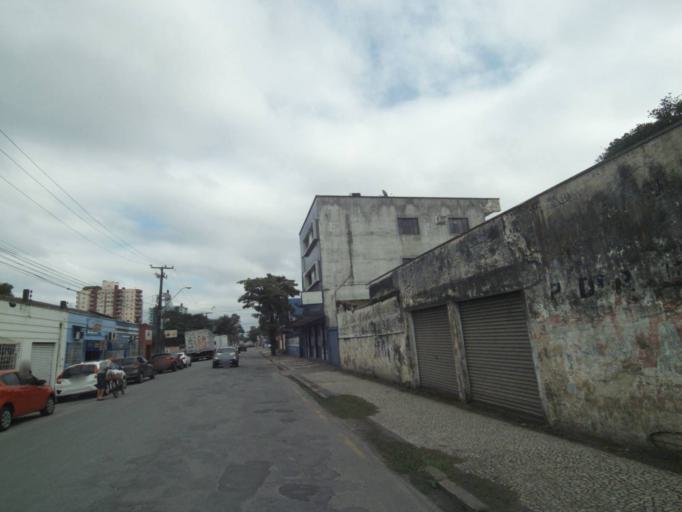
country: BR
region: Parana
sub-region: Paranagua
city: Paranagua
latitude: -25.5182
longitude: -48.5097
